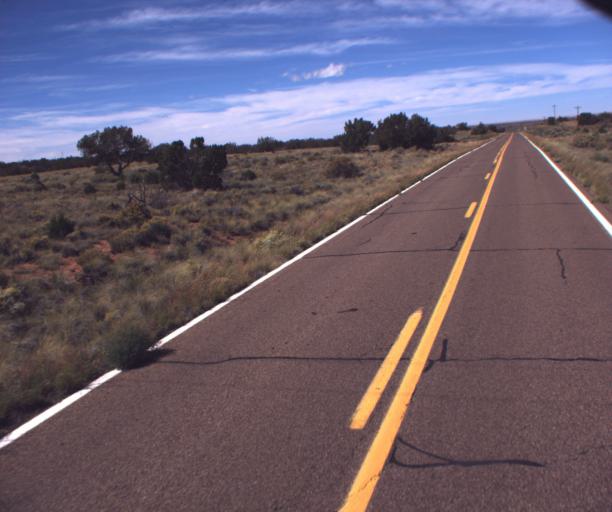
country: US
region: Arizona
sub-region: Apache County
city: Saint Johns
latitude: 34.6137
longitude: -109.6597
